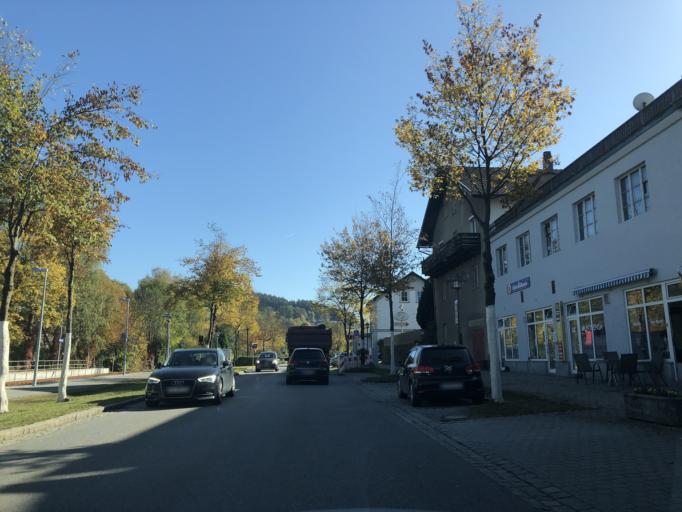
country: DE
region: Bavaria
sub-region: Lower Bavaria
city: Teisnach
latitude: 49.0393
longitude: 12.9940
